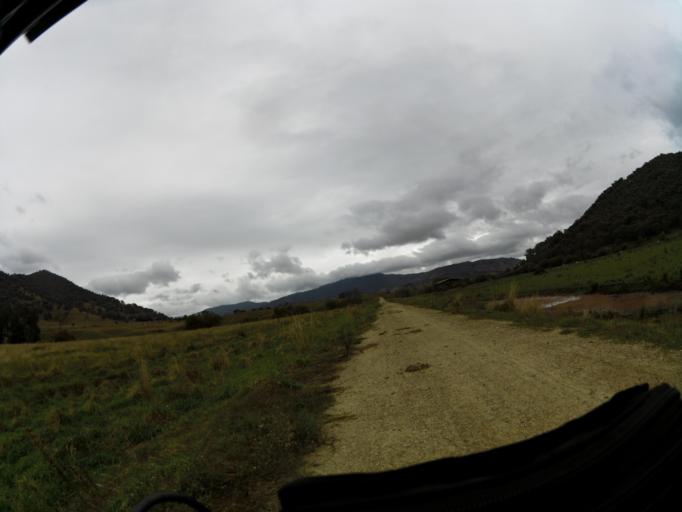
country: AU
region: New South Wales
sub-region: Albury Municipality
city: East Albury
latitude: -36.1831
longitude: 147.3430
